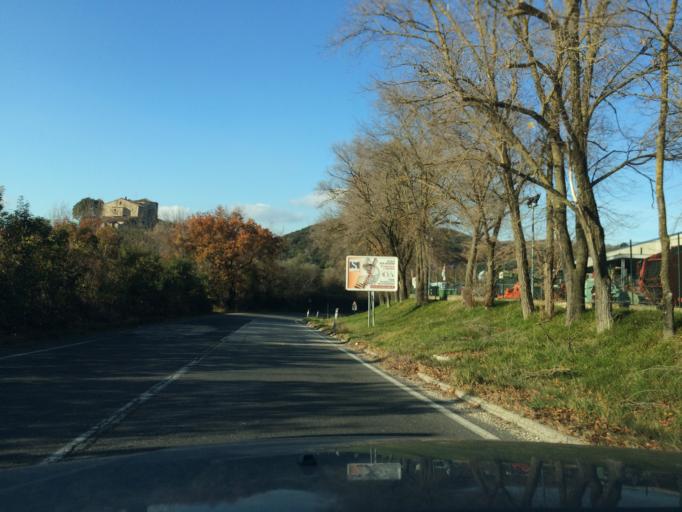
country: IT
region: Umbria
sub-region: Provincia di Terni
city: Fornole
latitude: 42.5486
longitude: 12.4483
